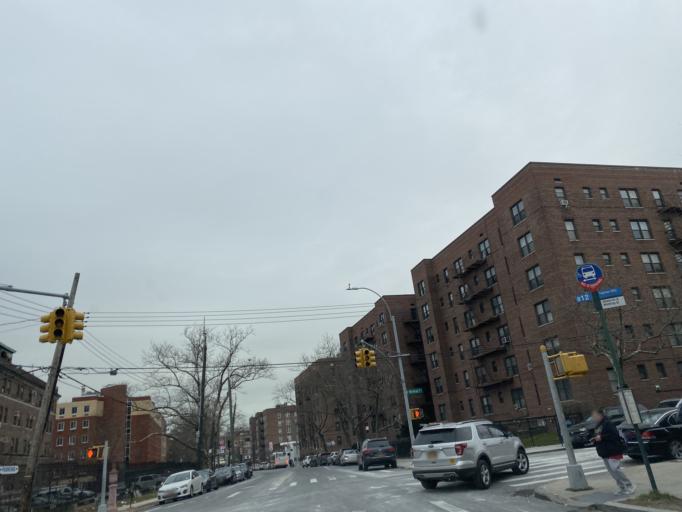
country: US
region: New York
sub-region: Kings County
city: Brooklyn
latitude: 40.6577
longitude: -73.9396
